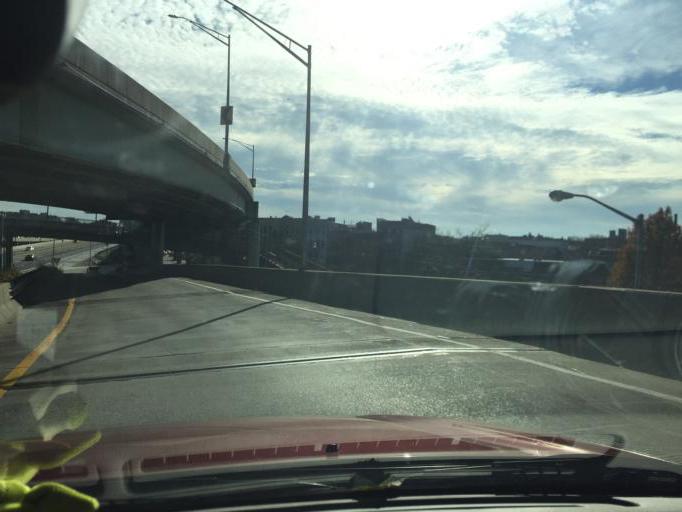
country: US
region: New York
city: New York City
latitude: 40.6791
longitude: -74.0039
